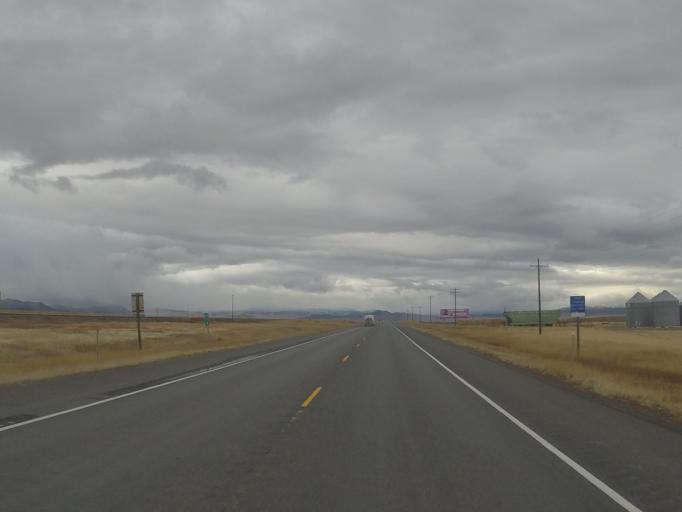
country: US
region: Montana
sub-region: Lewis and Clark County
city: East Helena
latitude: 46.5722
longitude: -111.8264
